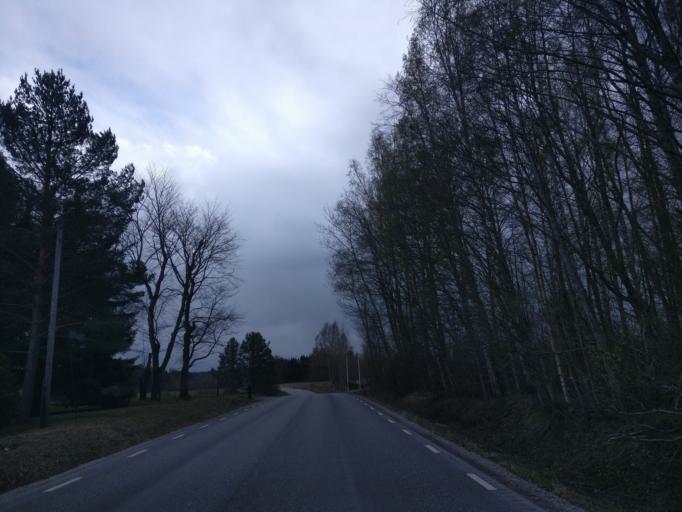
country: SE
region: Vaesternorrland
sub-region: Sundsvalls Kommun
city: Skottsund
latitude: 62.2828
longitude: 17.3948
